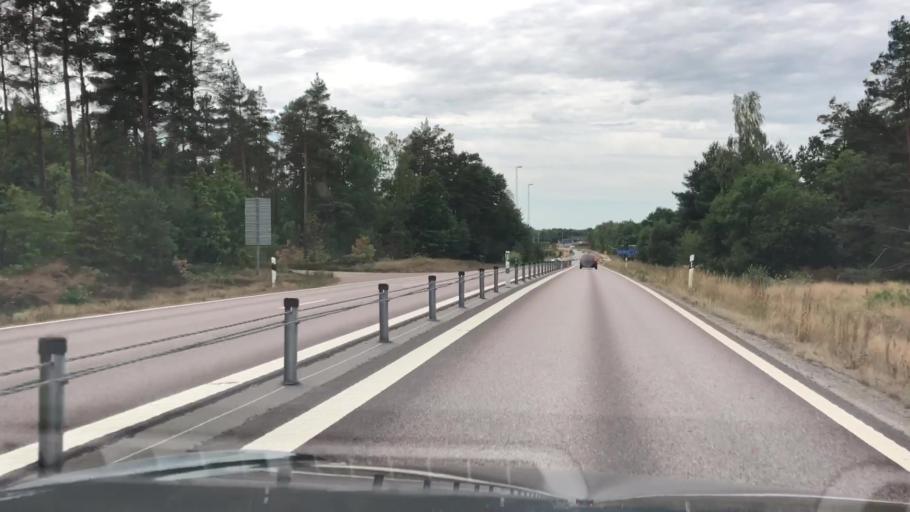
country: SE
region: Blekinge
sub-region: Karlskrona Kommun
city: Jaemjoe
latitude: 56.2022
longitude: 15.8589
